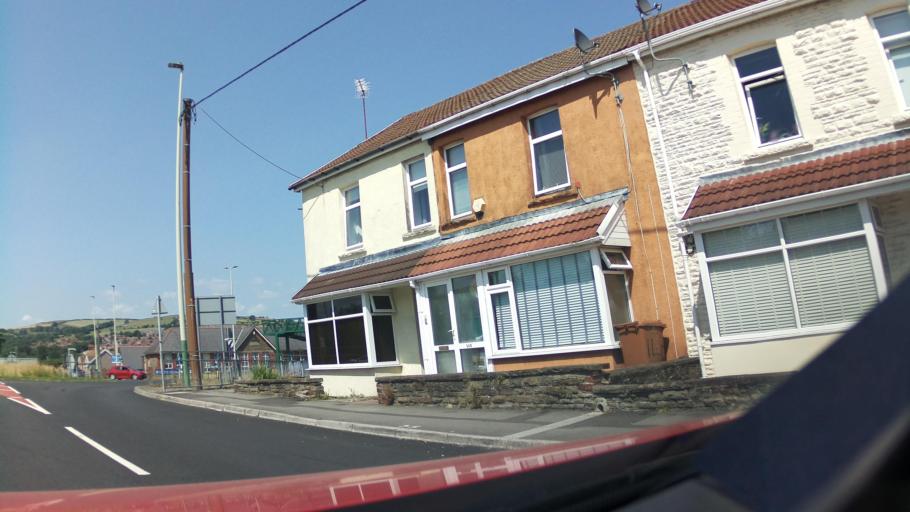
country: GB
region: Wales
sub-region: Caerphilly County Borough
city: Caerphilly
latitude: 51.5794
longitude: -3.2392
